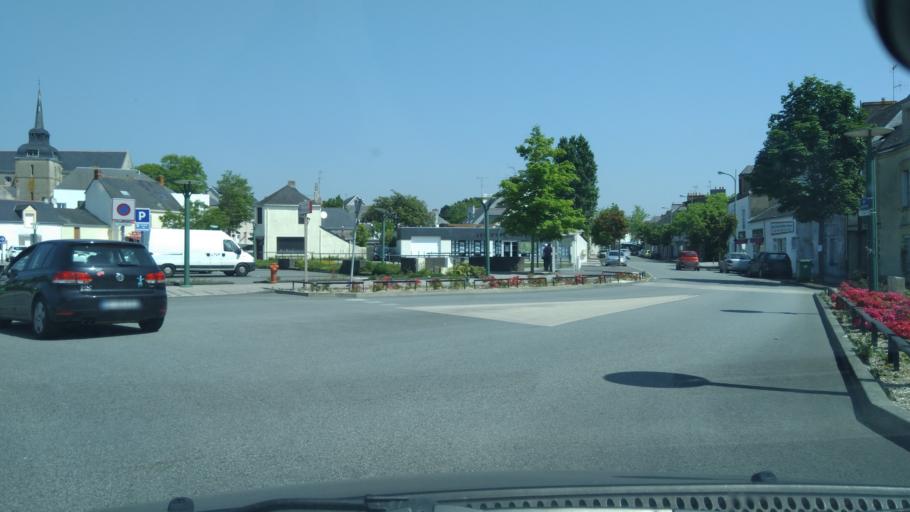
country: FR
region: Pays de la Loire
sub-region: Departement de la Loire-Atlantique
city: Montoir-de-Bretagne
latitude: 47.3266
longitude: -2.1560
